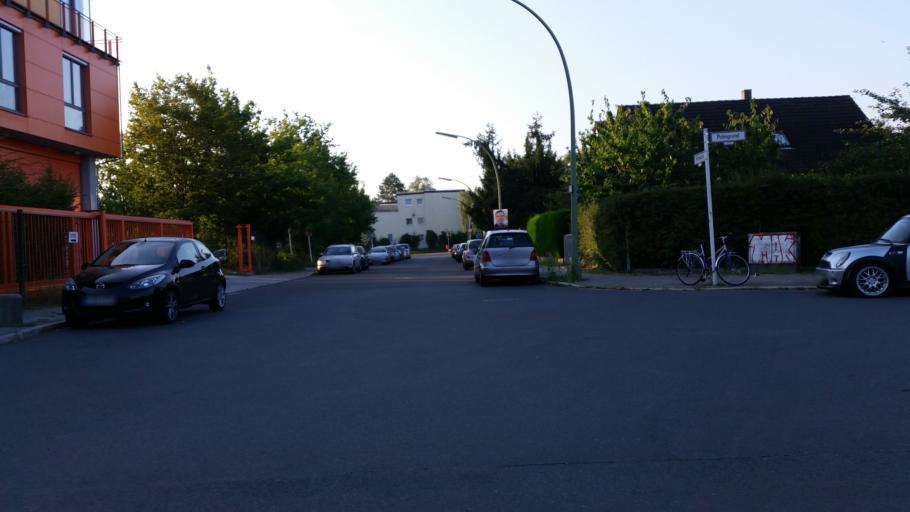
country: DE
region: Berlin
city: Lichtenrade
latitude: 52.3993
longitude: 13.3878
